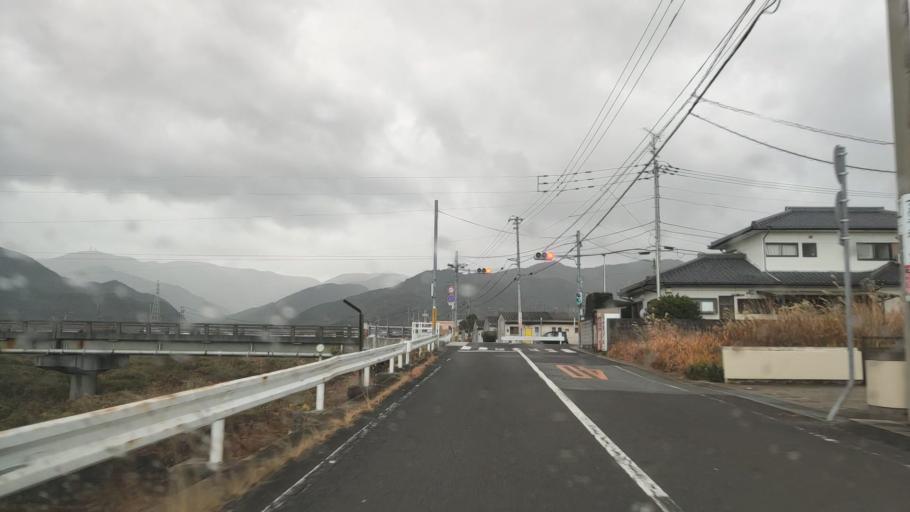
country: JP
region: Tokushima
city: Ishii
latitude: 34.2171
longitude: 134.4079
